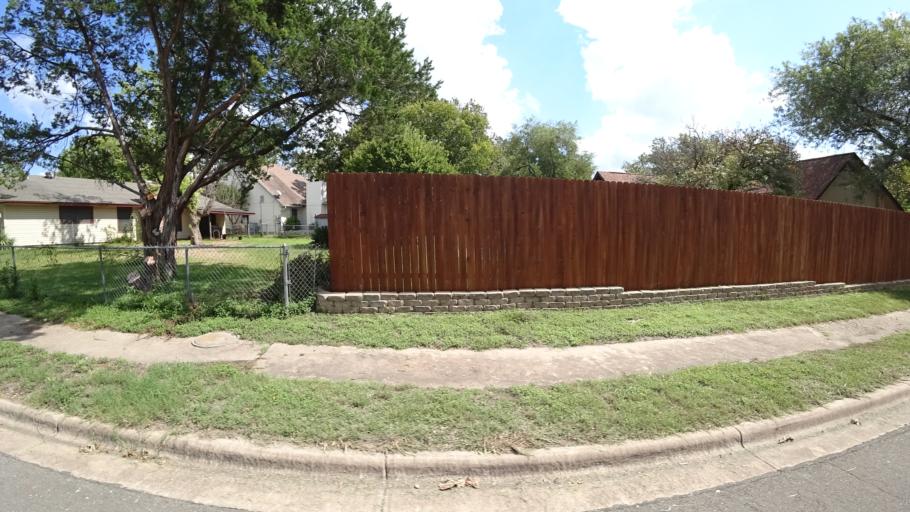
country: US
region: Texas
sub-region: Travis County
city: Onion Creek
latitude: 30.1928
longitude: -97.7897
